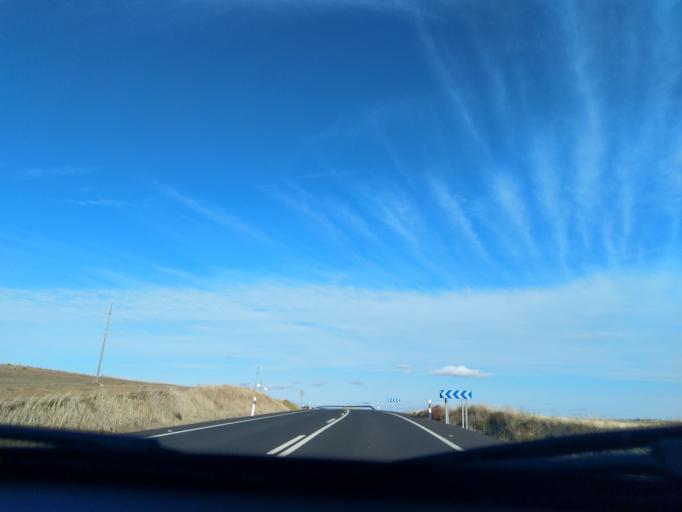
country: ES
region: Extremadura
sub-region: Provincia de Badajoz
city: Ahillones
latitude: 38.2649
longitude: -5.8519
